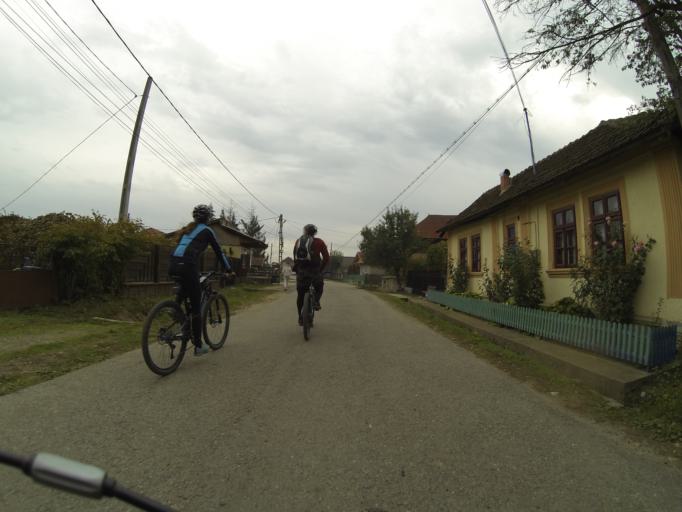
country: RO
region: Gorj
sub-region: Comuna Tismana
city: Pocruia
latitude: 45.0454
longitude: 22.9227
